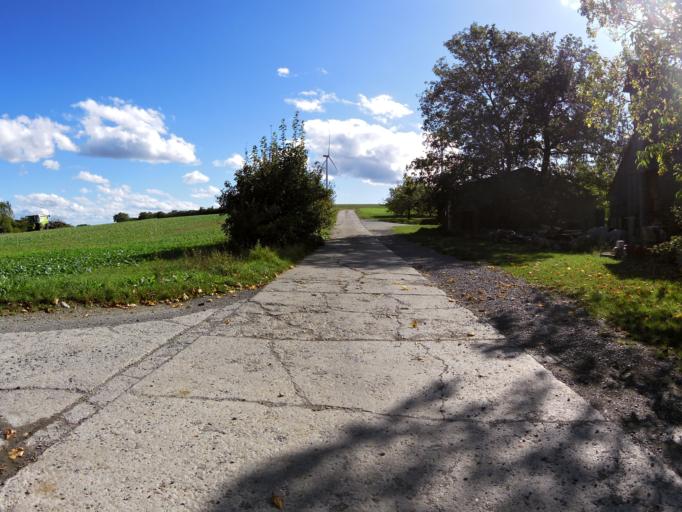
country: DE
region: Bavaria
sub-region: Regierungsbezirk Unterfranken
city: Erlabrunn
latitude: 49.8402
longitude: 9.8275
